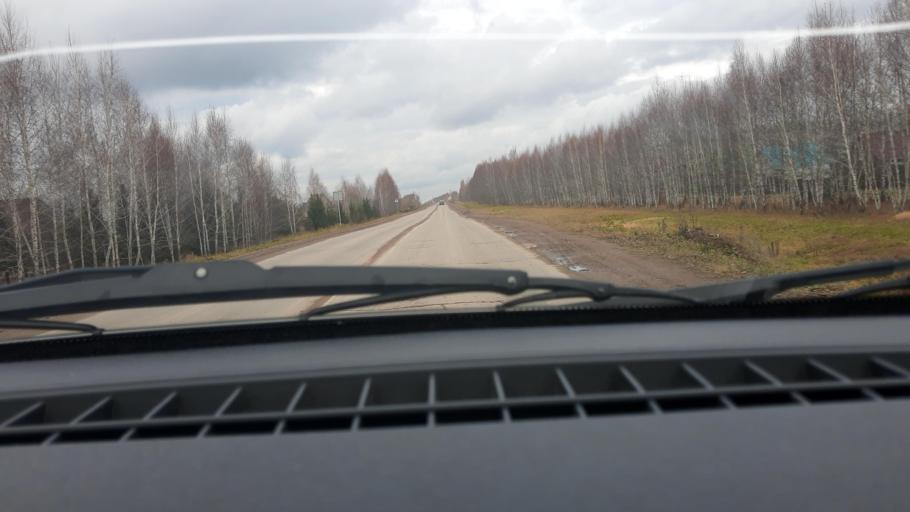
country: RU
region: Bashkortostan
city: Iglino
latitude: 54.8147
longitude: 56.4163
